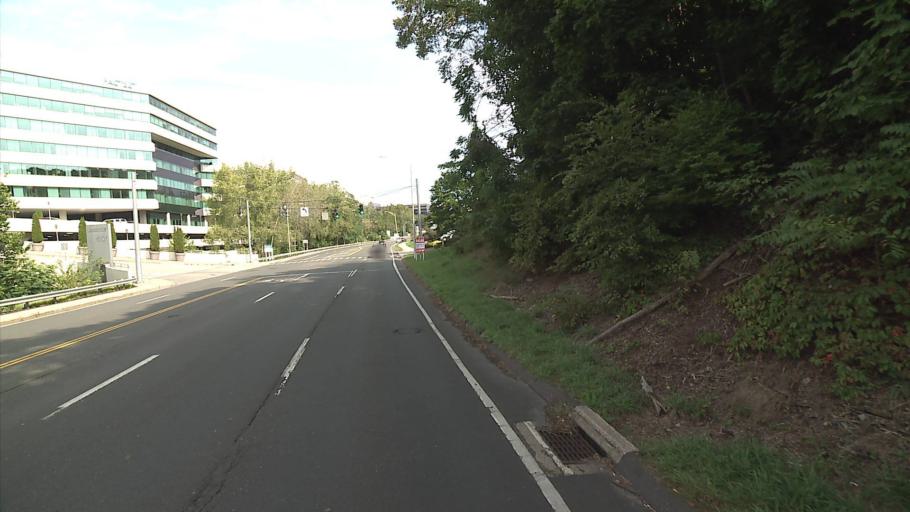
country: US
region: Connecticut
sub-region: Fairfield County
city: Norwalk
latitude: 41.1457
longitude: -73.4263
